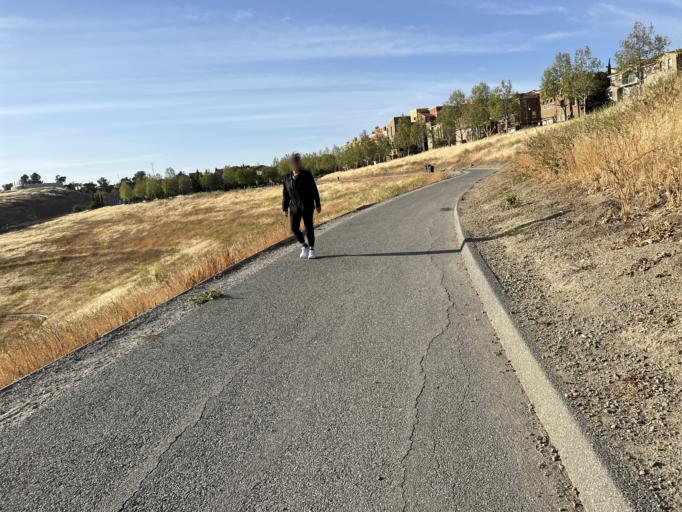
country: US
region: California
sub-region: Santa Clara County
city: Seven Trees
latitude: 37.2842
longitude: -121.8604
